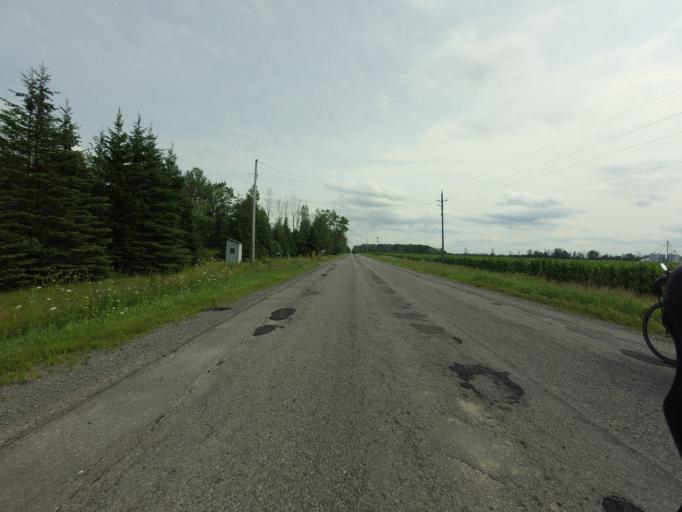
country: CA
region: Ontario
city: Bells Corners
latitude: 45.1127
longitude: -75.5984
